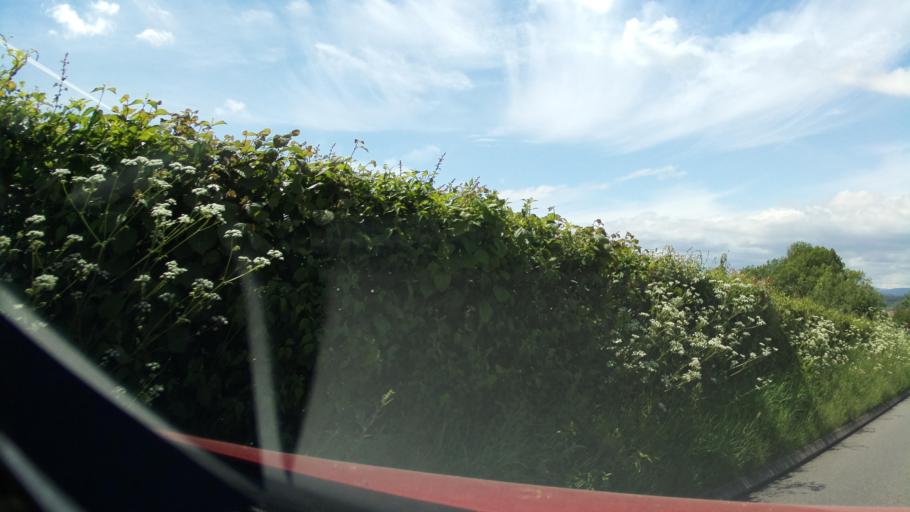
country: GB
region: Wales
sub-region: Monmouthshire
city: Mitchel Troy
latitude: 51.7874
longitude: -2.7173
